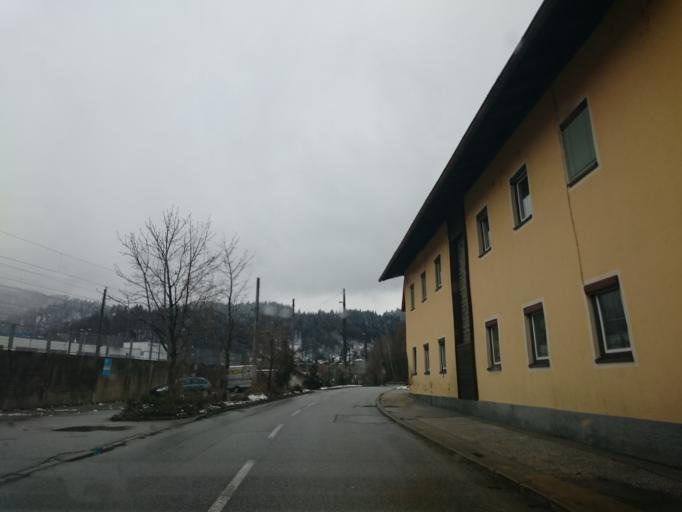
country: AT
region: Tyrol
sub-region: Politischer Bezirk Kufstein
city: Kufstein
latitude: 47.5852
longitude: 12.1662
